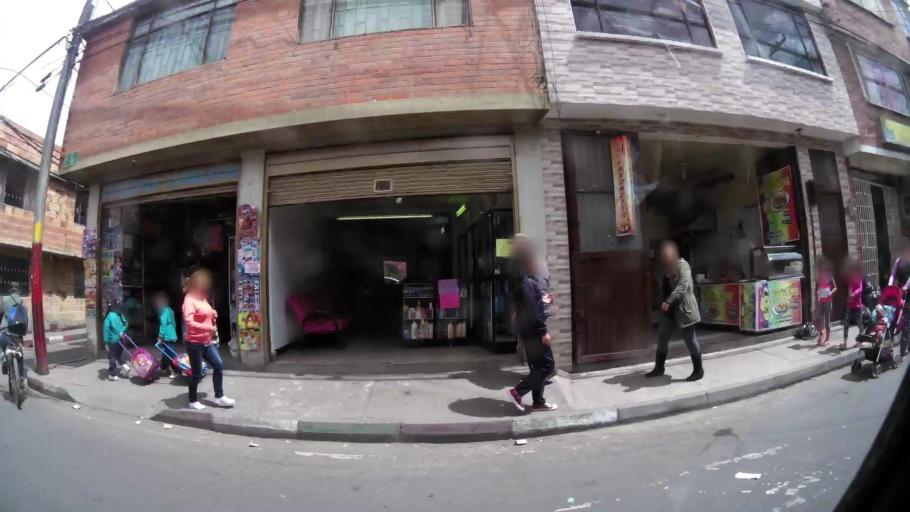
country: CO
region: Cundinamarca
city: Funza
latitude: 4.7153
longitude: -74.1395
